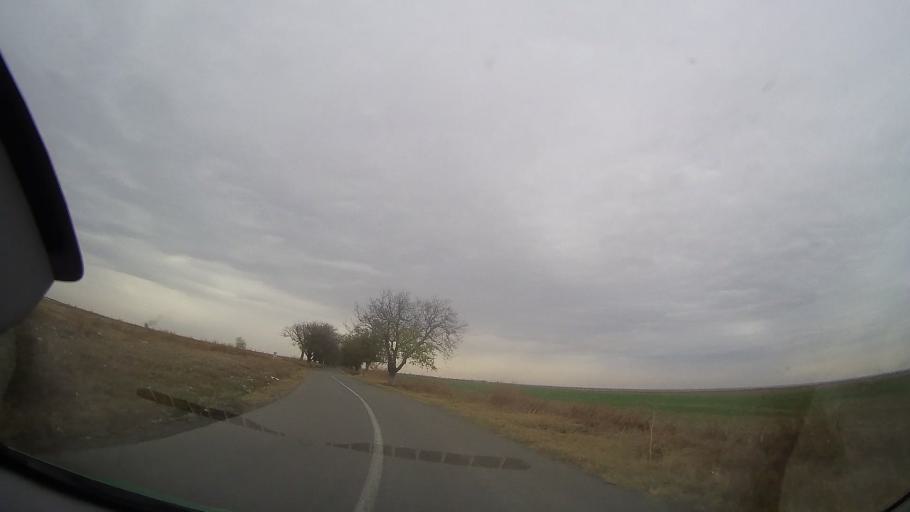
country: RO
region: Prahova
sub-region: Comuna Vadu Sapat
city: Vadu Sapat
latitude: 45.0195
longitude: 26.3952
